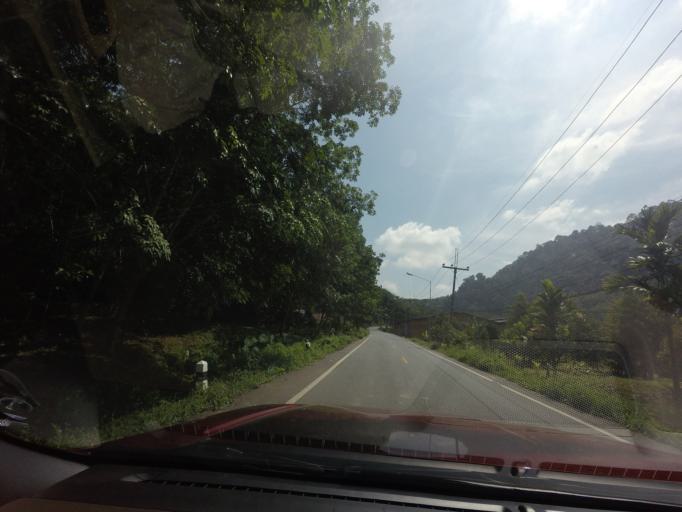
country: TH
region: Yala
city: Betong
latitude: 5.8297
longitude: 101.0785
